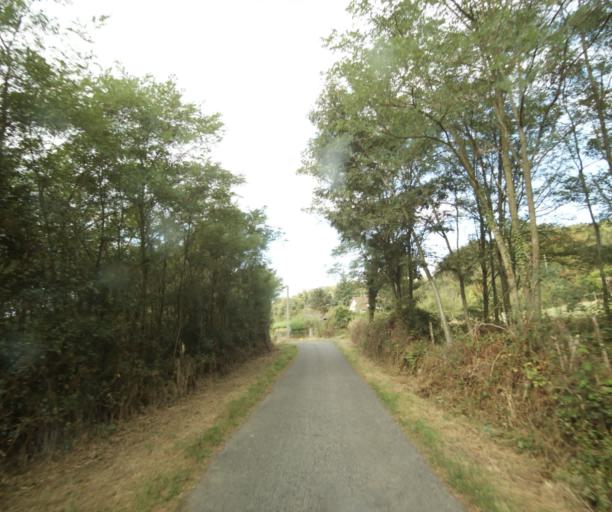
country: FR
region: Bourgogne
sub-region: Departement de Saone-et-Loire
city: Palinges
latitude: 46.5232
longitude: 4.2915
